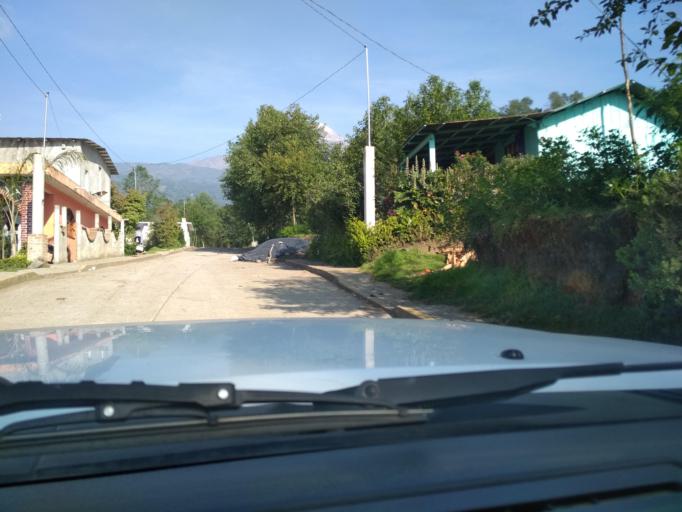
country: MX
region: Veracruz
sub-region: La Perla
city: Chilapa
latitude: 18.9851
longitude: -97.1647
